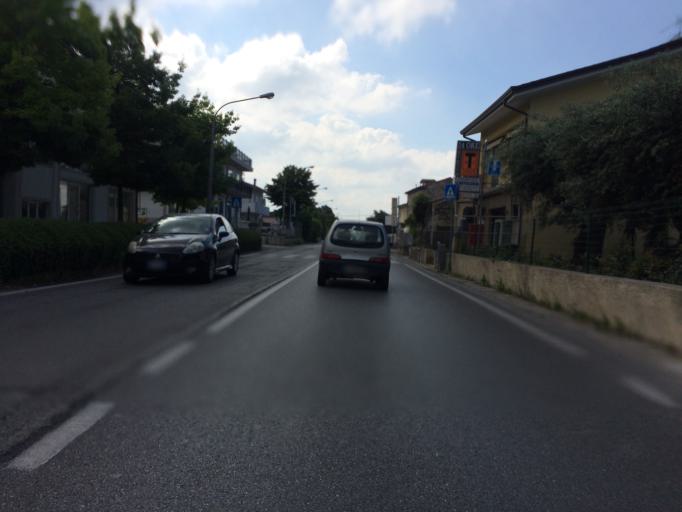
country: IT
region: Tuscany
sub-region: Provincia di Lucca
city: Ripa-Pozzi-Querceta-Ponterosso
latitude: 43.9720
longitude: 10.2064
